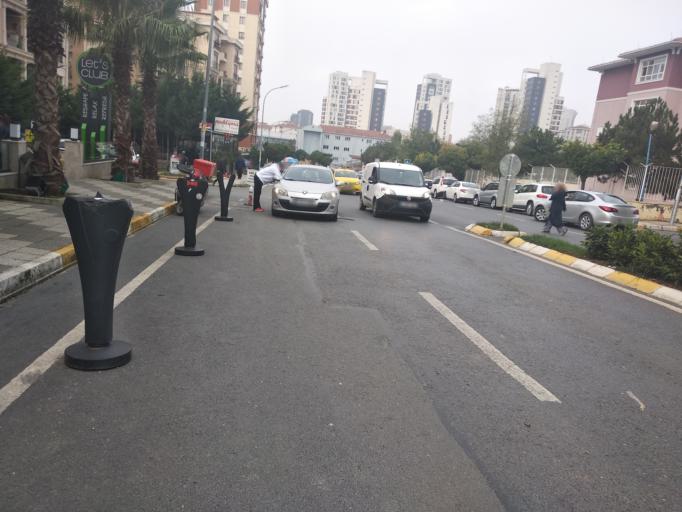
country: TR
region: Istanbul
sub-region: Atasehir
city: Atasehir
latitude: 40.9831
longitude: 29.1248
